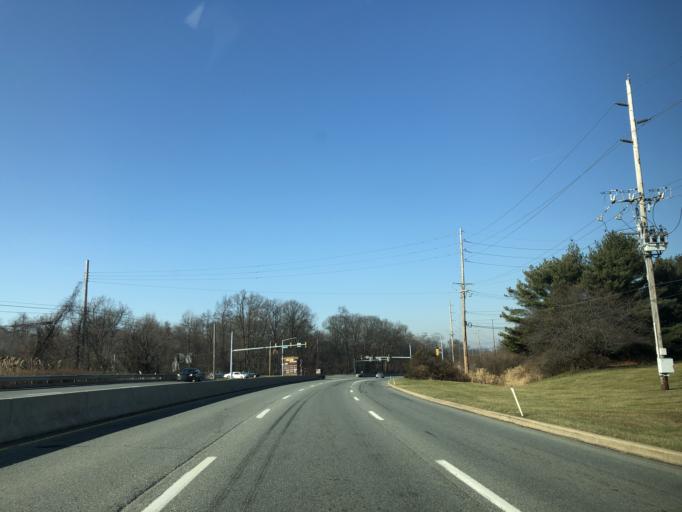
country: US
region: Pennsylvania
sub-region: Chester County
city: Exton
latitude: 40.0577
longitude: -75.6618
